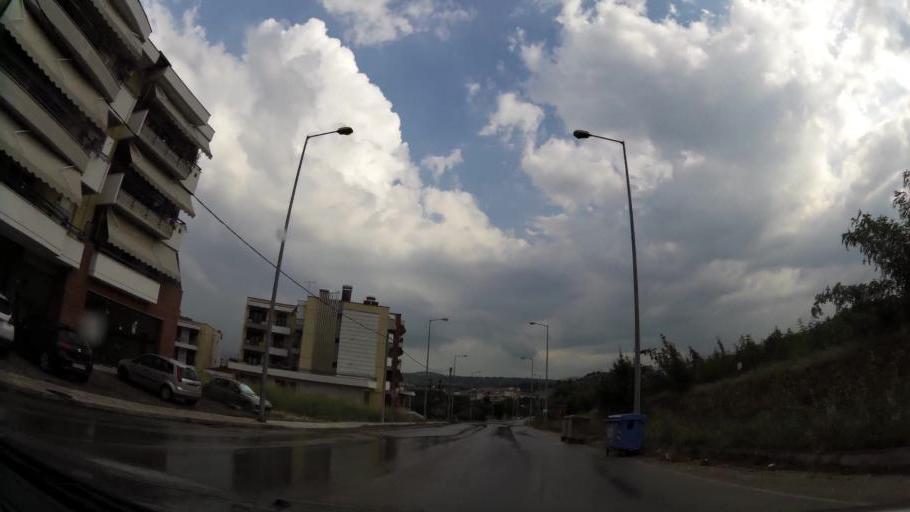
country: GR
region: Central Macedonia
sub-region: Nomos Imathias
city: Veroia
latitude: 40.5374
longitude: 22.1971
